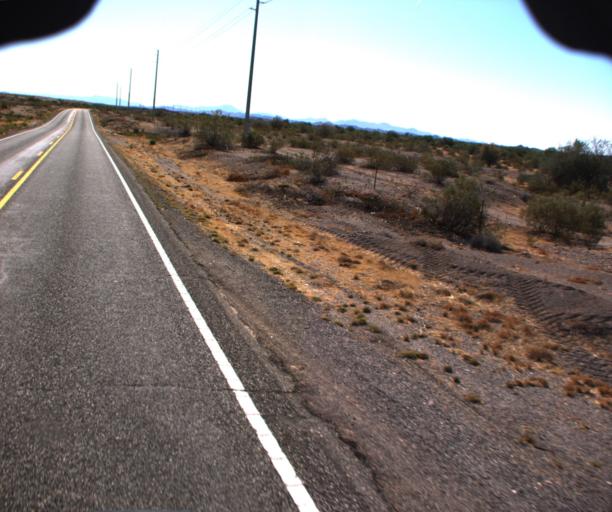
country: US
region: Arizona
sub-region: La Paz County
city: Cienega Springs
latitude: 33.9939
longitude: -114.1009
